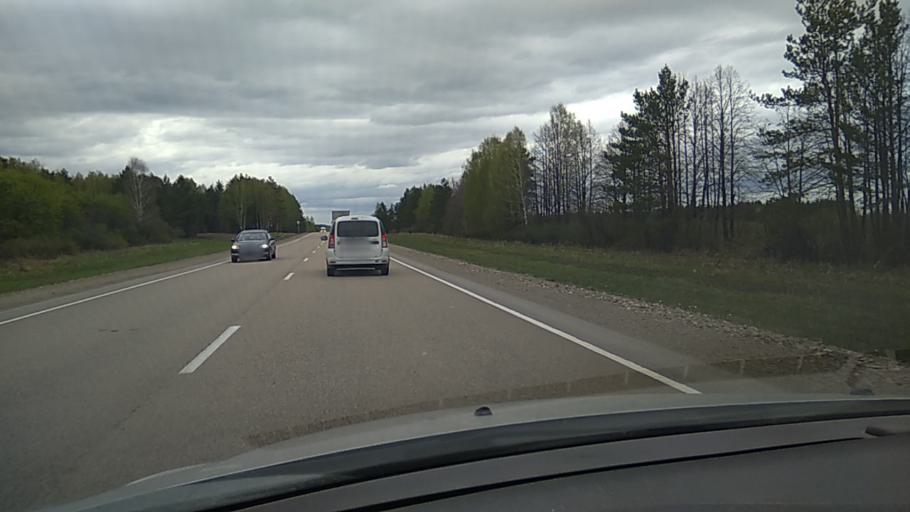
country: RU
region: Sverdlovsk
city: Dvurechensk
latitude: 56.6789
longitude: 61.1297
